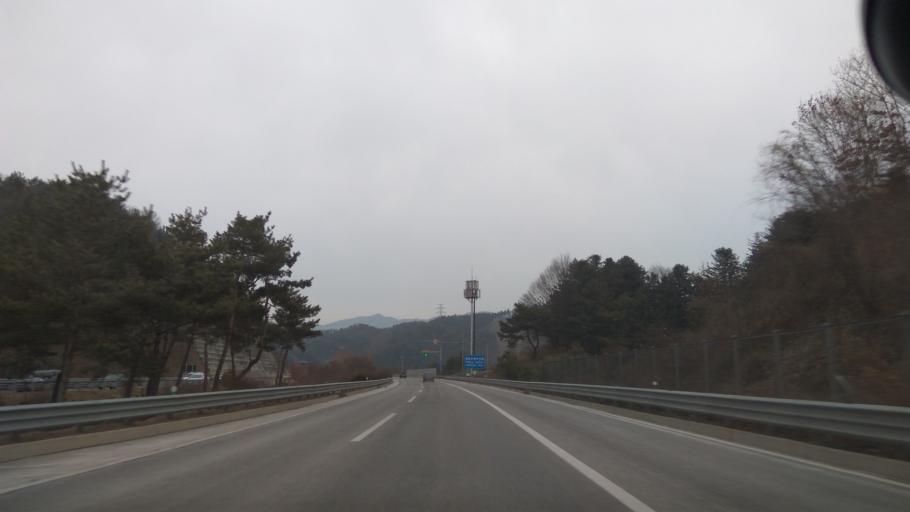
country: KR
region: Gyeonggi-do
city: Cheongpyeong
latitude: 37.6518
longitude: 127.4820
